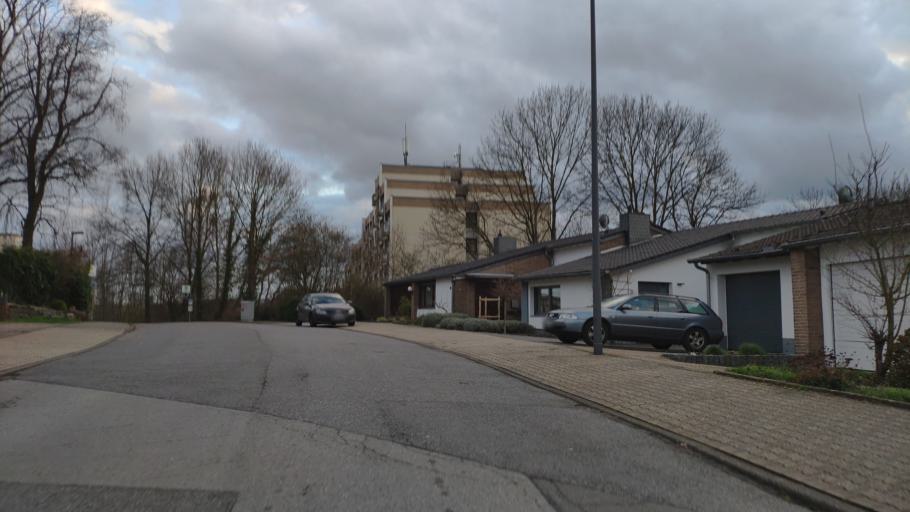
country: DE
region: North Rhine-Westphalia
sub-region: Regierungsbezirk Koln
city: Aachen
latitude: 50.8025
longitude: 6.0652
